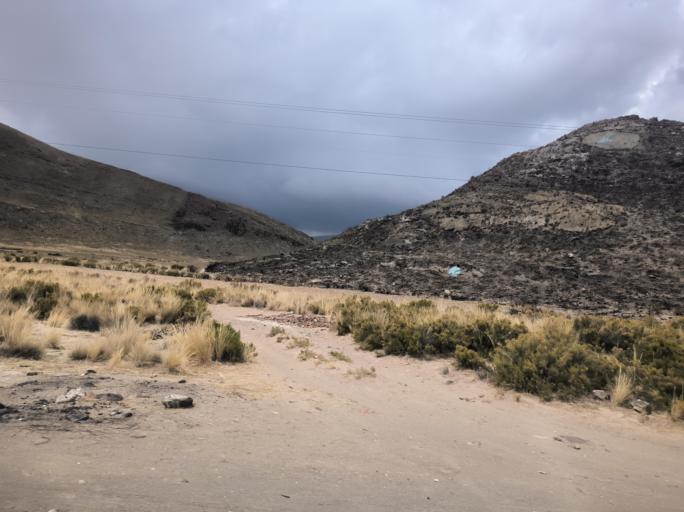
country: BO
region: Oruro
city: Challapata
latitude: -18.7494
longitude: -66.8643
